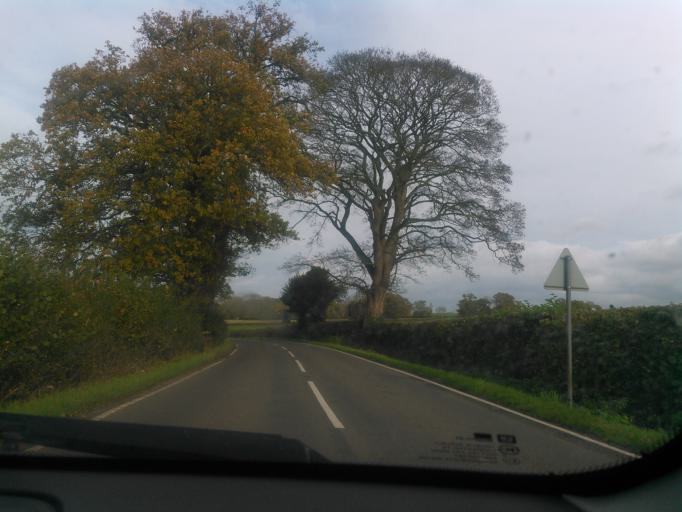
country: GB
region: England
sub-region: Shropshire
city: Clive
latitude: 52.8222
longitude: -2.7394
